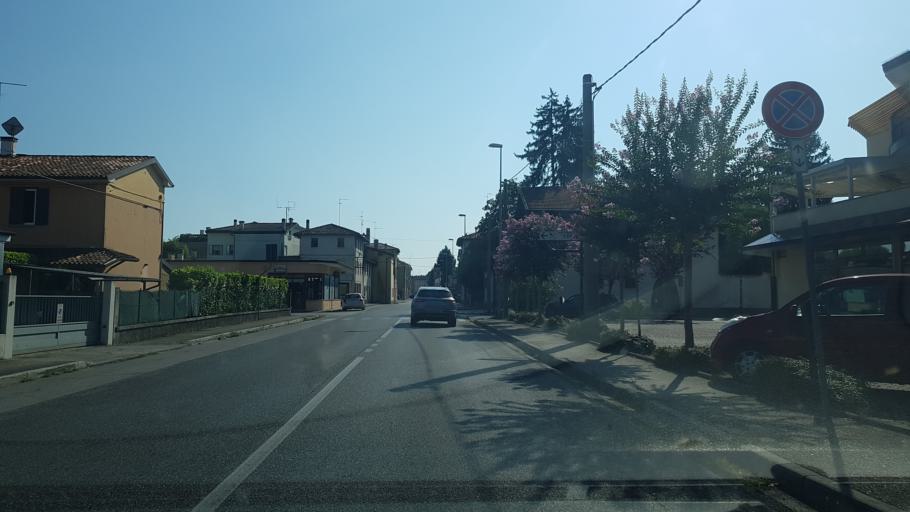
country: IT
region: Friuli Venezia Giulia
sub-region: Provincia di Udine
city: Latisana
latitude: 45.7802
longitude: 12.9990
